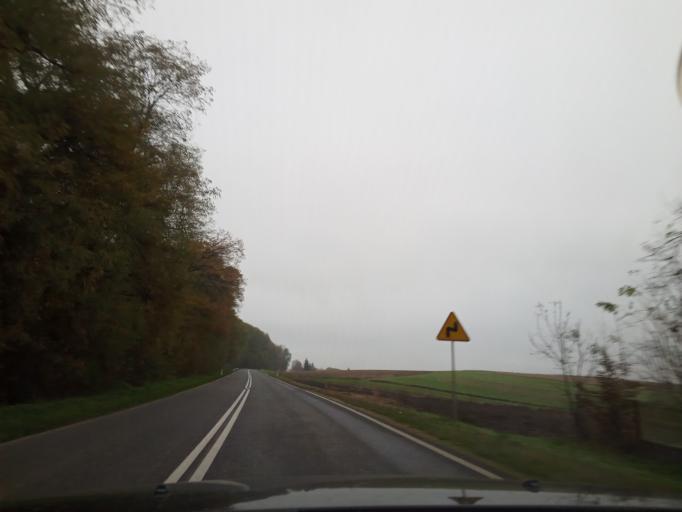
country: PL
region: Lesser Poland Voivodeship
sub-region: Powiat proszowicki
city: Klimontow
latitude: 50.2323
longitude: 20.3872
